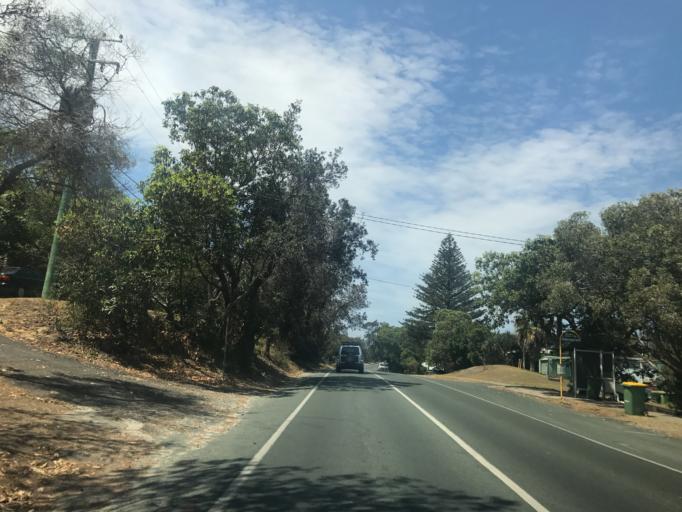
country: AU
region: Queensland
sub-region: Redland
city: Victoria Point
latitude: -27.4283
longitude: 153.5384
